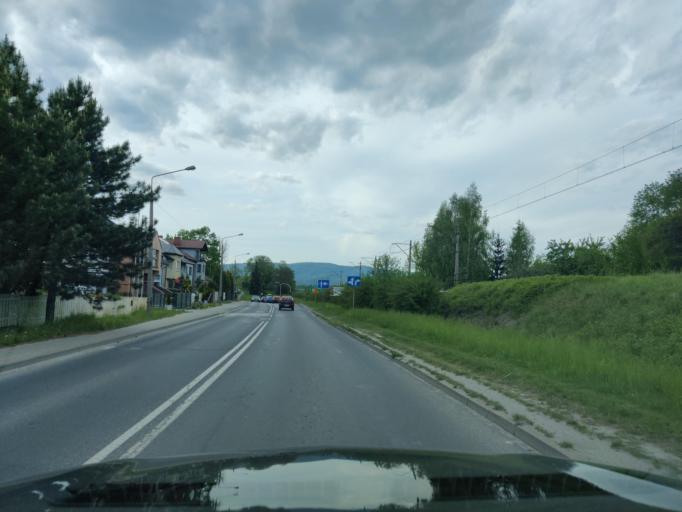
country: PL
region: Silesian Voivodeship
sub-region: Powiat zywiecki
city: Zywiec
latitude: 49.6838
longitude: 19.1871
